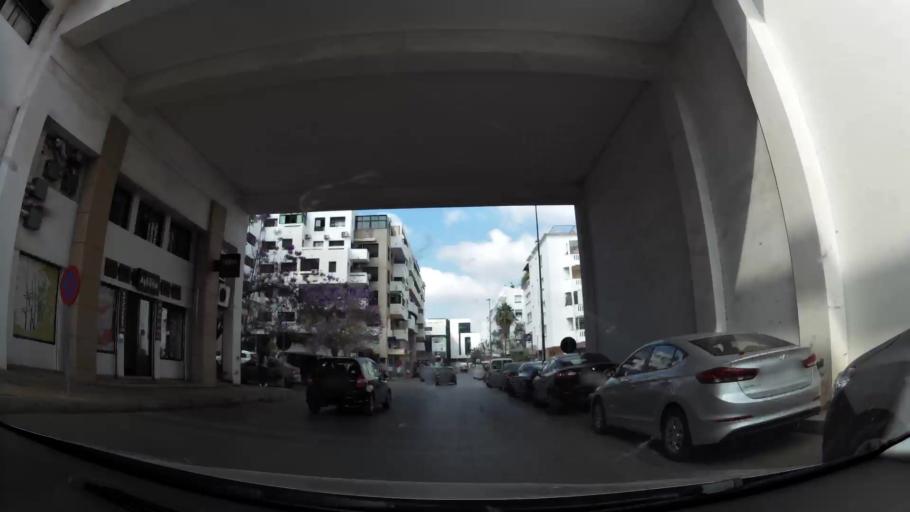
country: MA
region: Rabat-Sale-Zemmour-Zaer
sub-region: Skhirate-Temara
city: Temara
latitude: 33.9602
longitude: -6.8671
